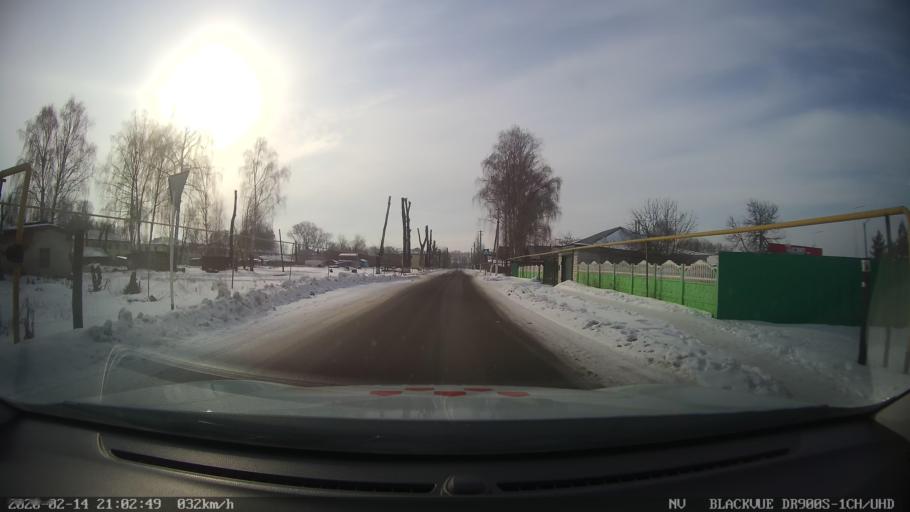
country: RU
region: Tatarstan
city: Kuybyshevskiy Zaton
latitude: 55.1591
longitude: 49.1777
